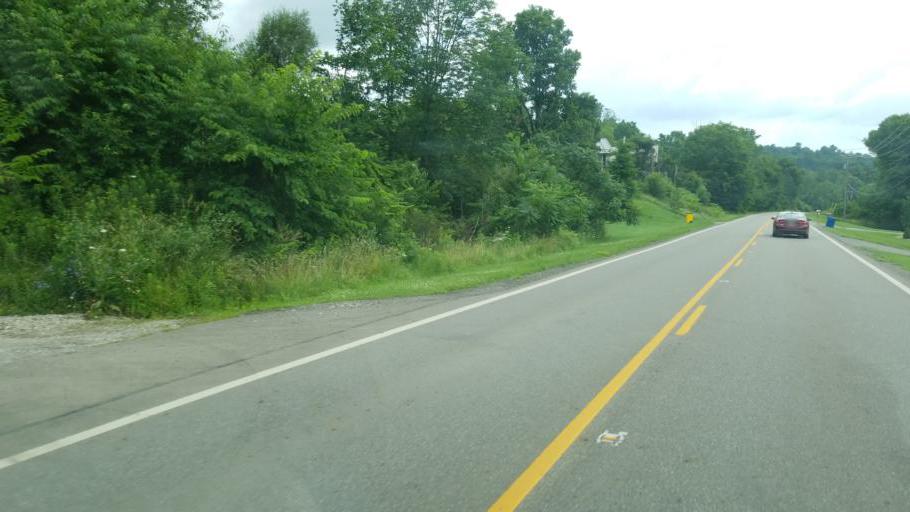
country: US
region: Ohio
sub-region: Columbiana County
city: Lisbon
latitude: 40.7602
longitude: -80.7853
